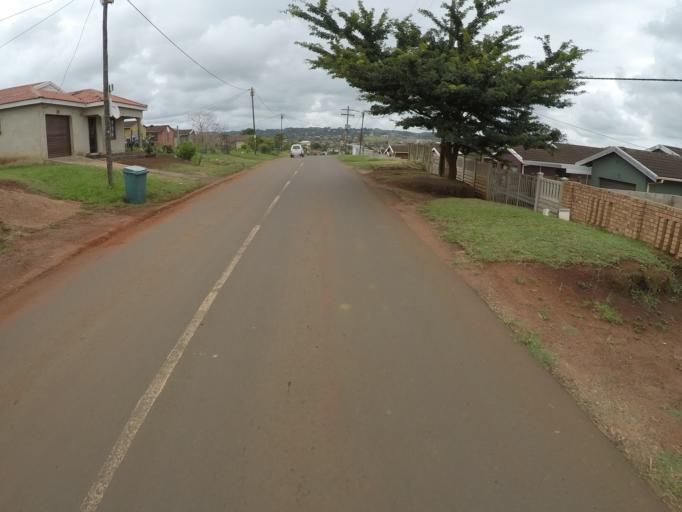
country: ZA
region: KwaZulu-Natal
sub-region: uThungulu District Municipality
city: Empangeni
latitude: -28.7729
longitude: 31.8807
